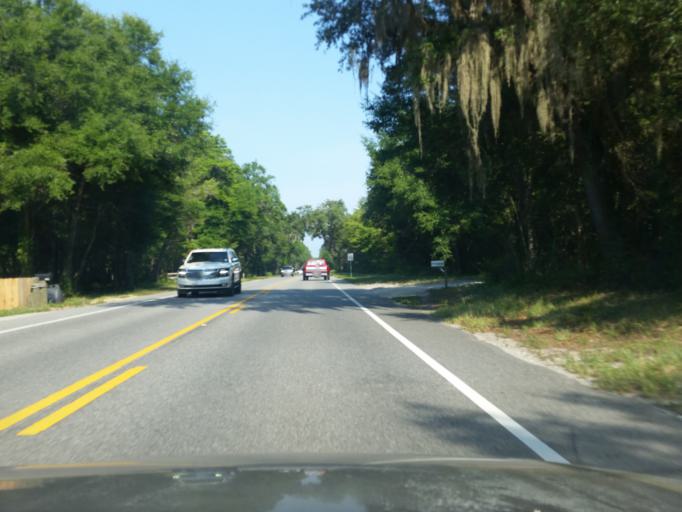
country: US
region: Alabama
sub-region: Baldwin County
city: Gulf Shores
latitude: 30.2517
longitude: -87.8033
